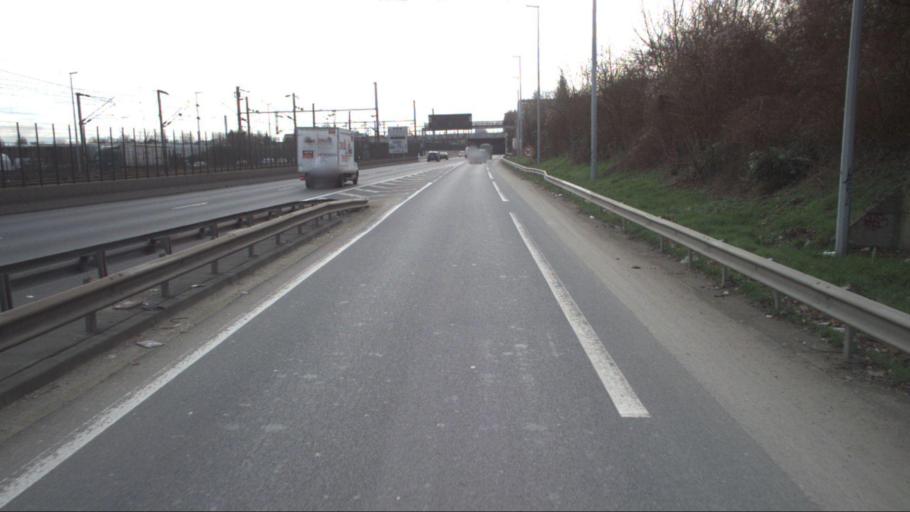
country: FR
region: Ile-de-France
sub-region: Departement du Val-de-Marne
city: Fontenay-sous-Bois
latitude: 48.8511
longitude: 2.4899
